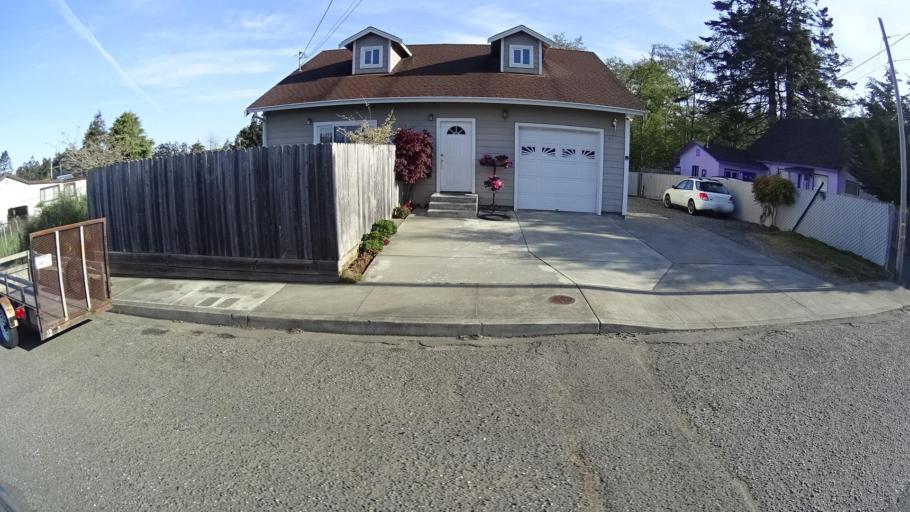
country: US
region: California
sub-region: Humboldt County
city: Bayview
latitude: 40.7656
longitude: -124.1789
